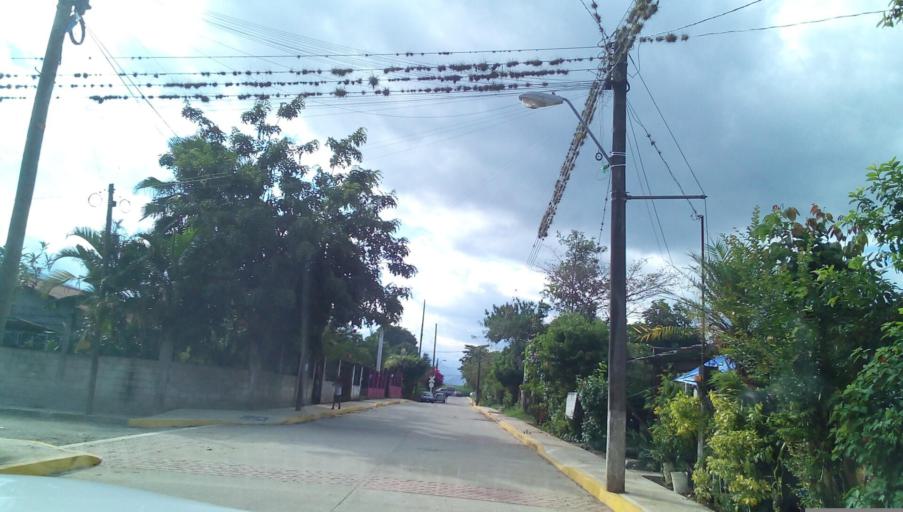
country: MX
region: Veracruz
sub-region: Amatlan de los Reyes
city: Centro de Readaptacion Social
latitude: 18.8247
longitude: -96.9225
